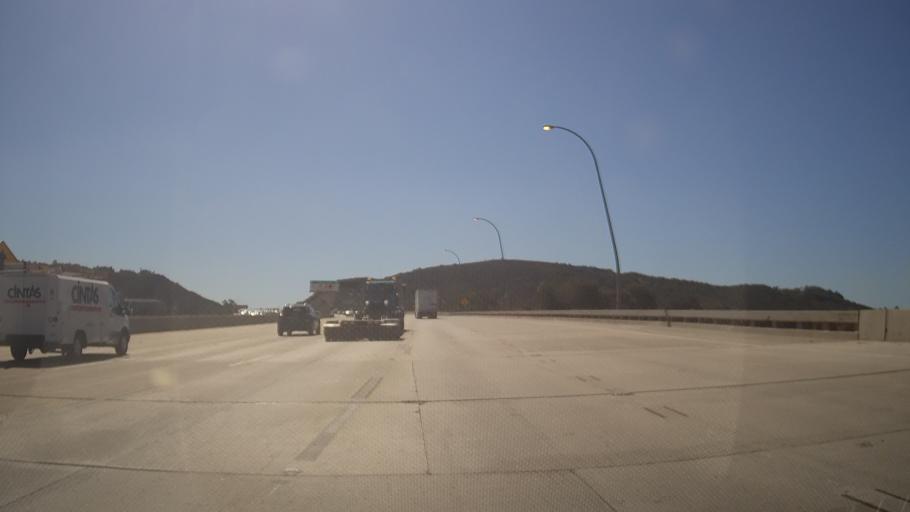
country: US
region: California
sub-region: San Diego County
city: Poway
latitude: 32.9463
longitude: -117.1081
